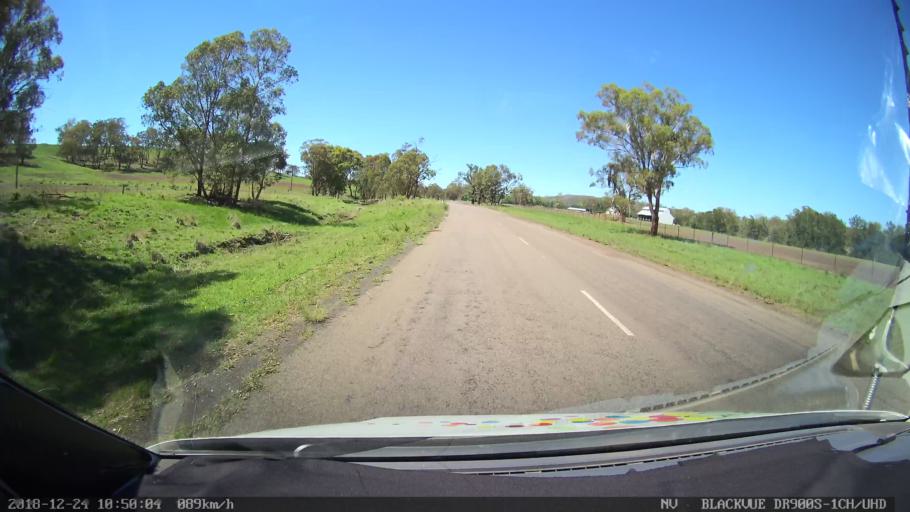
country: AU
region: New South Wales
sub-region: Upper Hunter Shire
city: Merriwa
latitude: -31.9553
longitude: 150.4248
